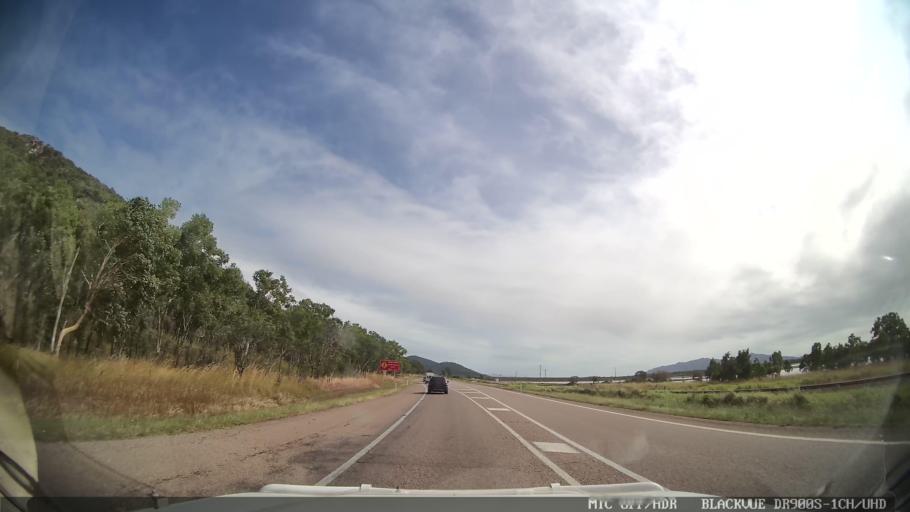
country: AU
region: Queensland
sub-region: Townsville
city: Townsville
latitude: -19.3984
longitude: 147.0233
